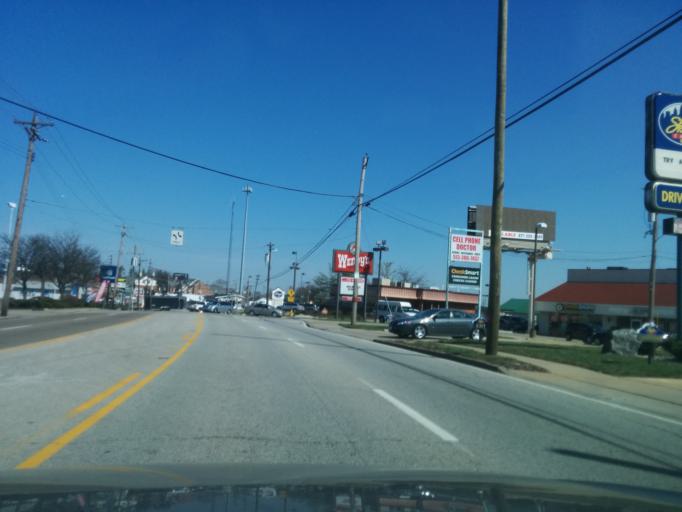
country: US
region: Ohio
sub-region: Hamilton County
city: Monfort Heights
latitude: 39.1892
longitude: -84.6006
